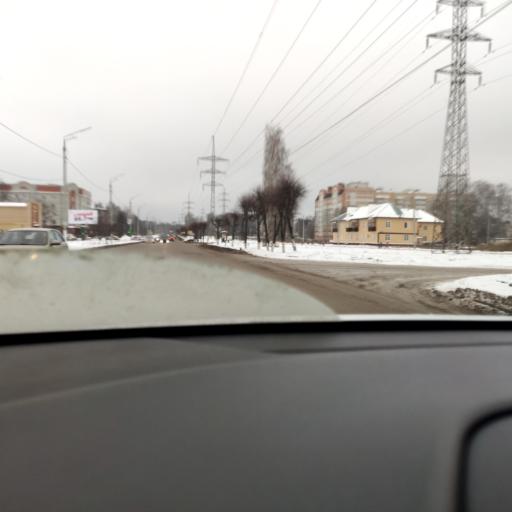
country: RU
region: Tatarstan
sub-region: Zelenodol'skiy Rayon
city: Zelenodolsk
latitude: 55.8532
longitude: 48.5019
